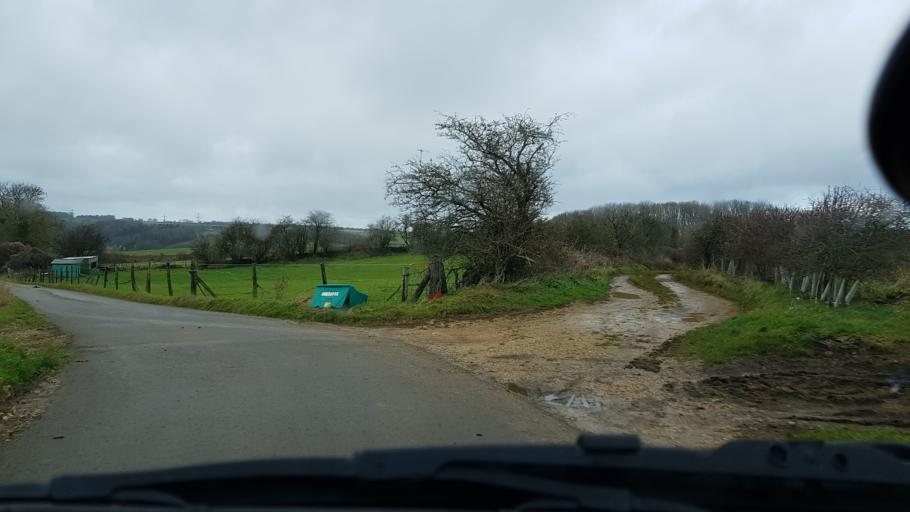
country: GB
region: England
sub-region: Gloucestershire
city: Charlton Kings
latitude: 51.8474
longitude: -2.0380
